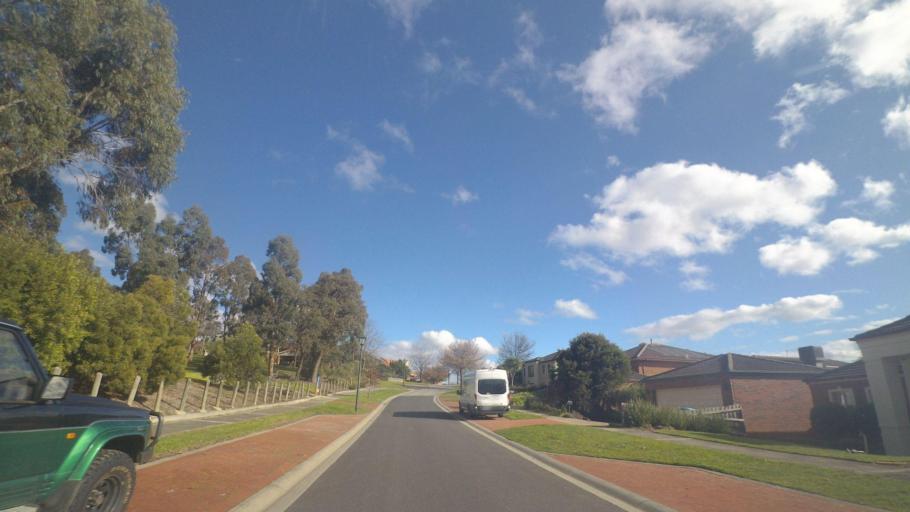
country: AU
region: Victoria
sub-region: Yarra Ranges
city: Lysterfield
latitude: -37.9220
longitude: 145.2782
